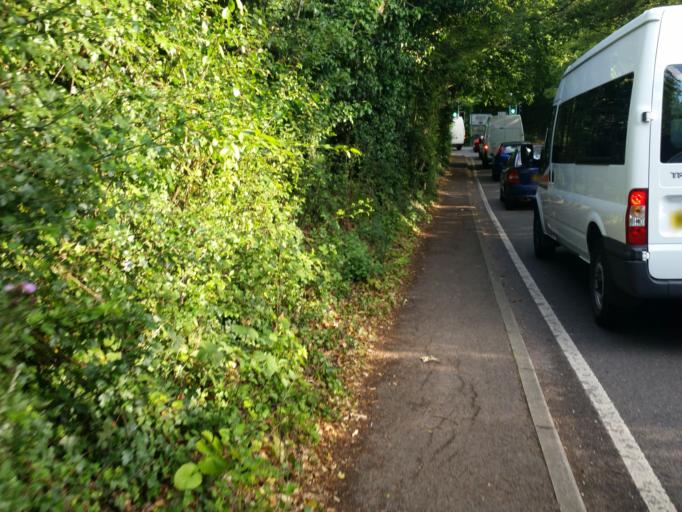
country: GB
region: England
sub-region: Greater London
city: Hendon
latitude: 51.6311
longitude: -0.2359
